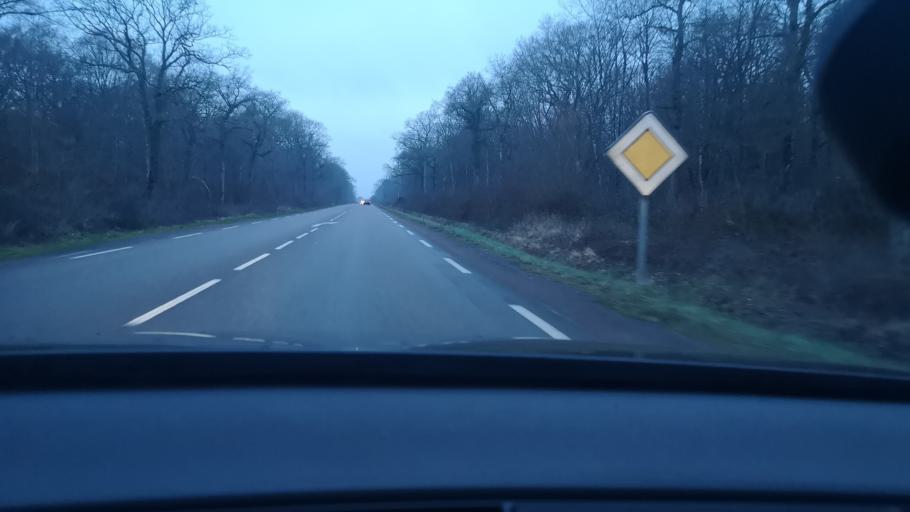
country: FR
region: Bourgogne
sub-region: Departement de Saone-et-Loire
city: Verdun-sur-le-Doubs
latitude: 47.0052
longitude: 5.0367
